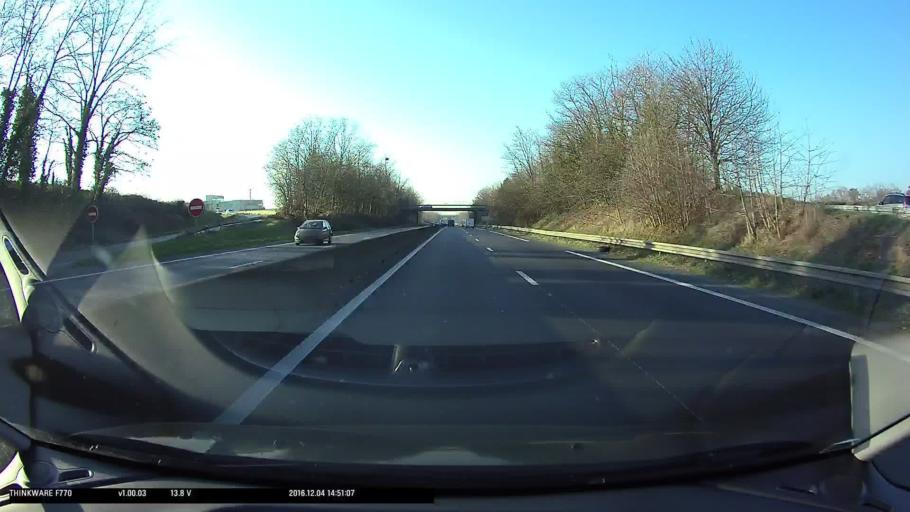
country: FR
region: Ile-de-France
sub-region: Departement du Val-d'Oise
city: Vaureal
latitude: 49.0584
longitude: 2.0334
